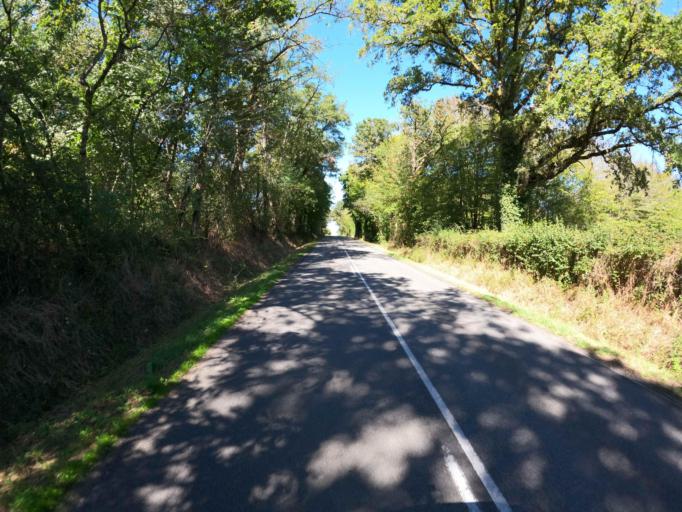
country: FR
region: Limousin
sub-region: Departement de la Haute-Vienne
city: Le Dorat
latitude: 46.2647
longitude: 1.0315
